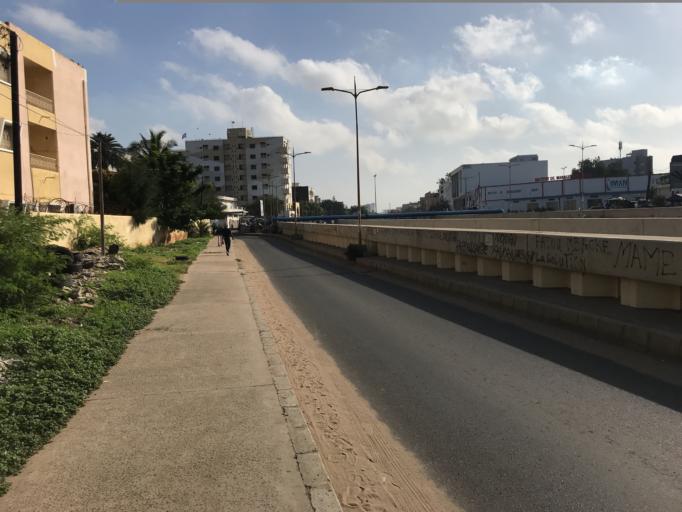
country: SN
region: Dakar
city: Dakar
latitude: 14.6895
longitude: -17.4591
